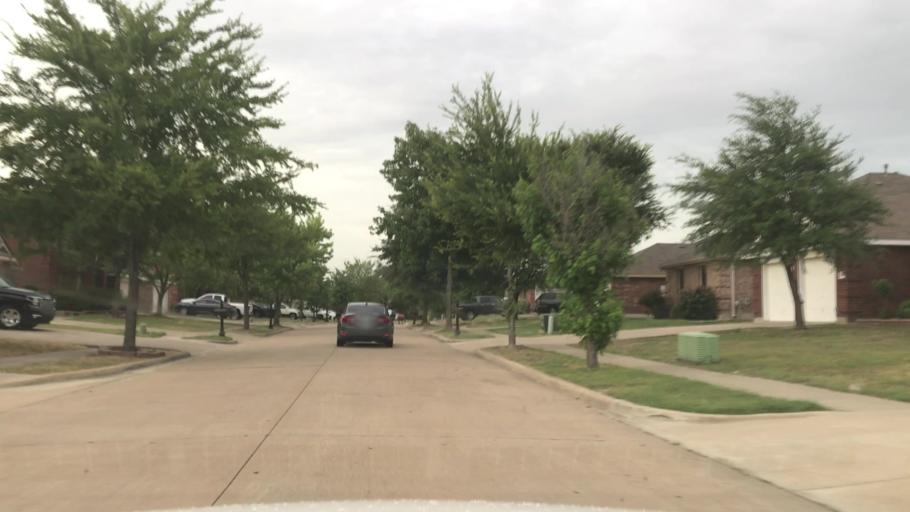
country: US
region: Texas
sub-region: Kaufman County
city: Forney
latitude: 32.7195
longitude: -96.5376
